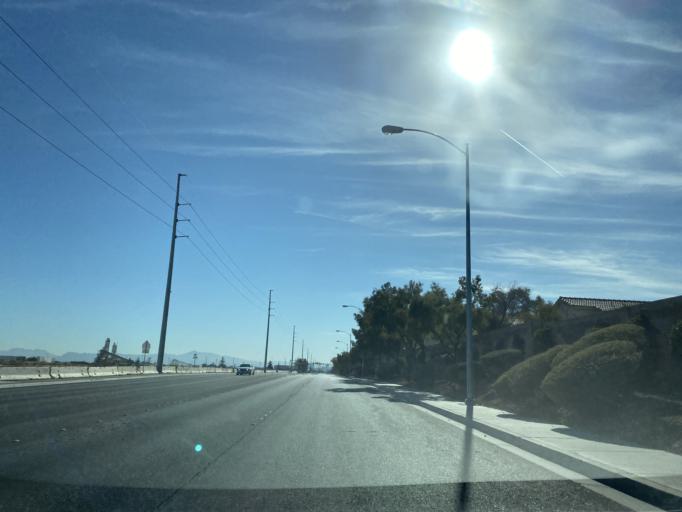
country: US
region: Nevada
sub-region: Clark County
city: North Las Vegas
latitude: 36.2283
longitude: -115.1434
